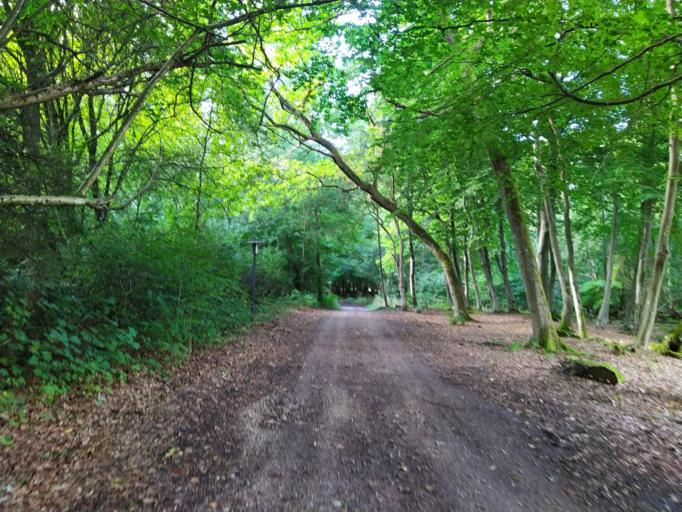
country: DK
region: Capital Region
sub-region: Egedal Kommune
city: Ganlose
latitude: 55.8113
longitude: 12.2745
